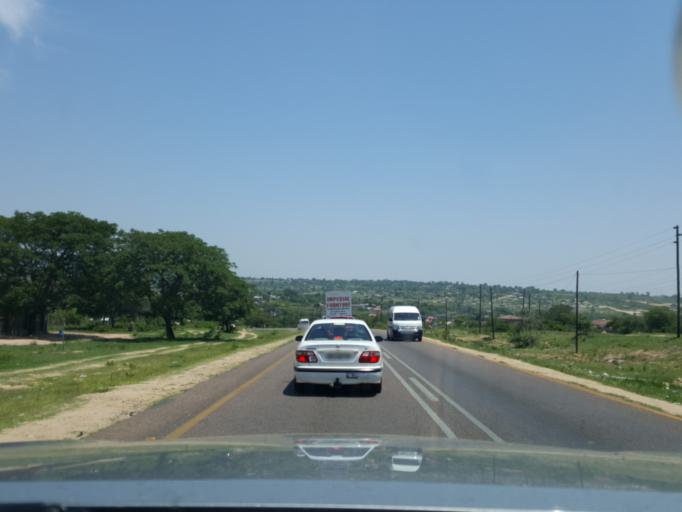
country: ZA
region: Limpopo
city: Thulamahashi
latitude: -24.7929
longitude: 31.0822
